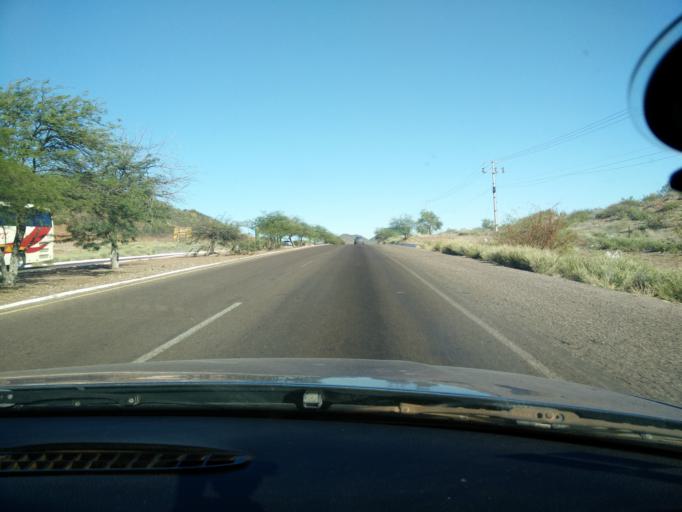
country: MX
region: Sonora
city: Heroica Guaymas
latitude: 27.9763
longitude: -110.9383
